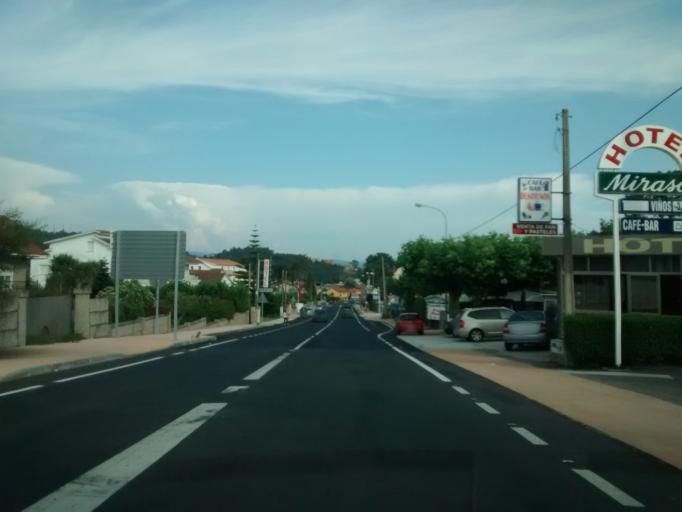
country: ES
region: Galicia
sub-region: Provincia de Pontevedra
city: Sanxenxo
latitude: 42.4215
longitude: -8.8734
